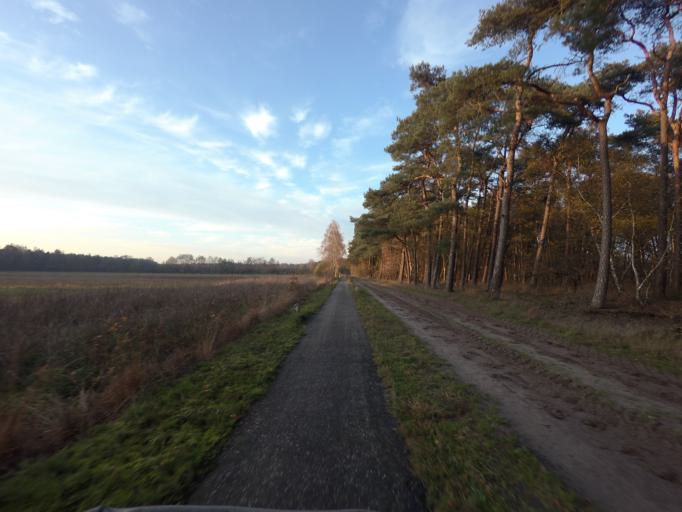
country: NL
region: North Brabant
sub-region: Gemeente Breda
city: Breda
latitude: 51.5186
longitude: 4.8123
